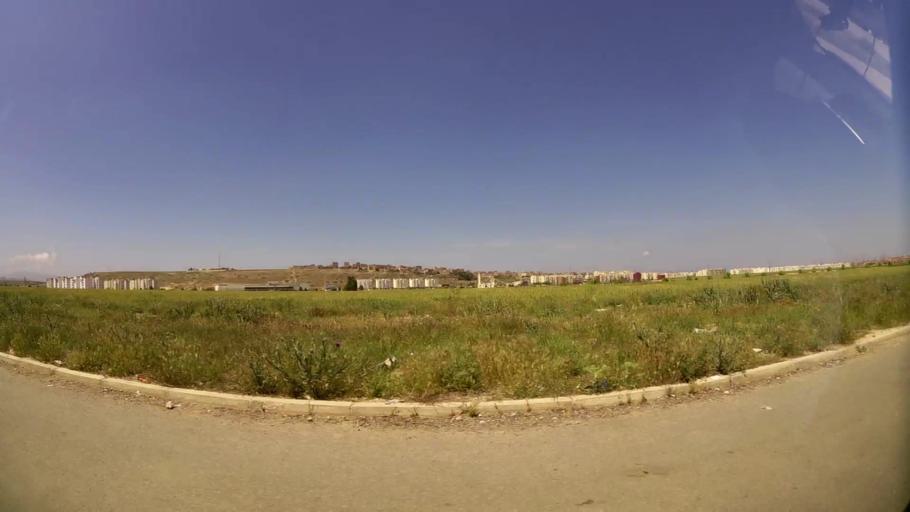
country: MA
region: Oriental
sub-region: Oujda-Angad
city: Oujda
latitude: 34.6954
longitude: -1.9391
